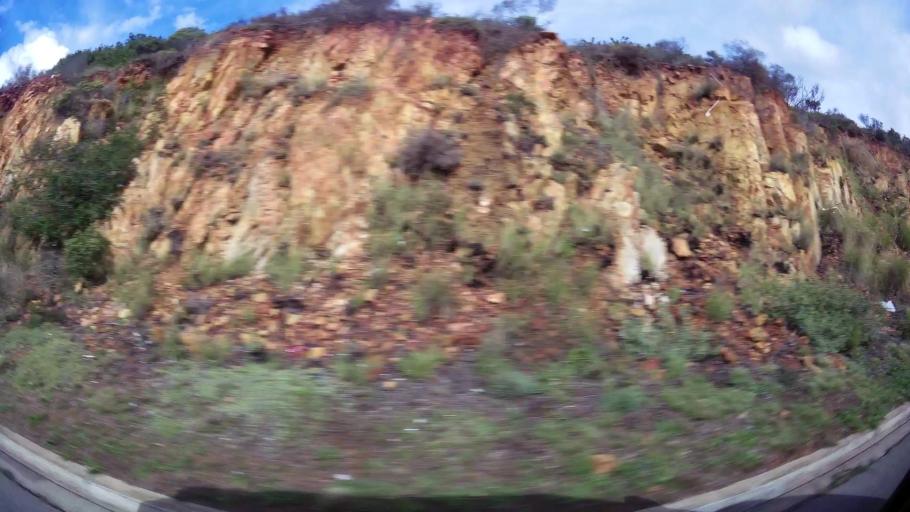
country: ZA
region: Eastern Cape
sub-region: Nelson Mandela Bay Metropolitan Municipality
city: Port Elizabeth
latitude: -33.9390
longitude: 25.5746
